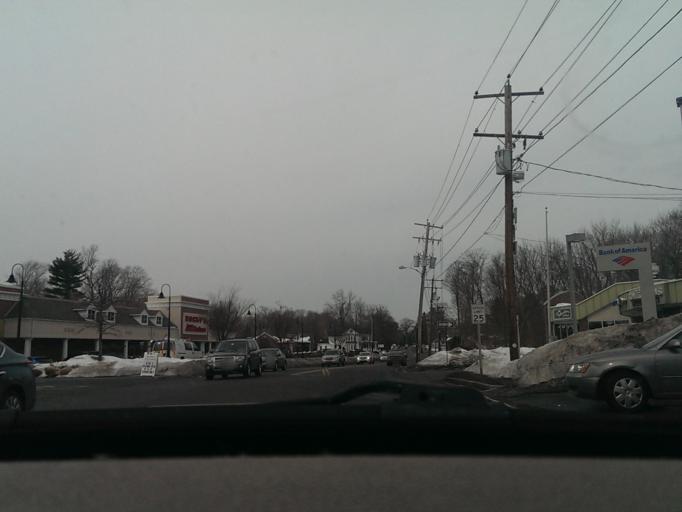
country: US
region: Massachusetts
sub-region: Hampden County
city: East Longmeadow
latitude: 42.0655
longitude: -72.5133
